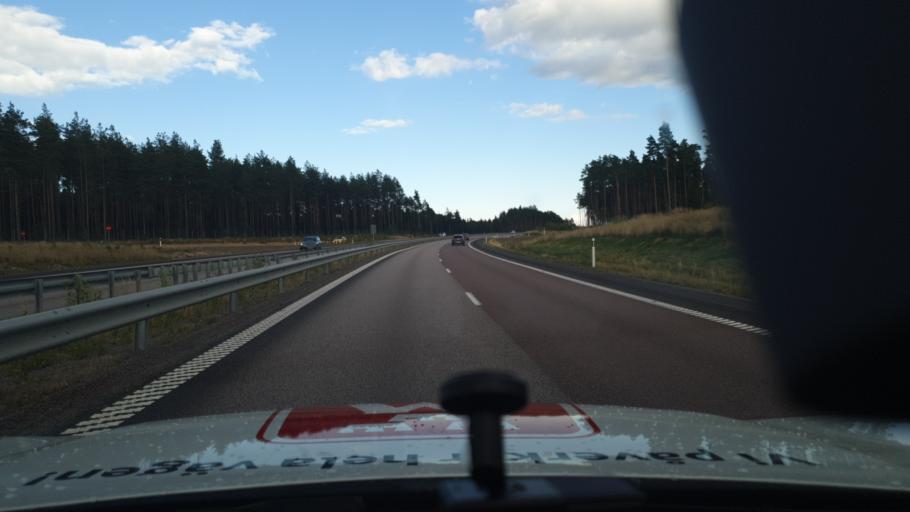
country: SE
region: Vaermland
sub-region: Karlstads Kommun
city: Edsvalla
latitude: 59.3925
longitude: 13.2843
